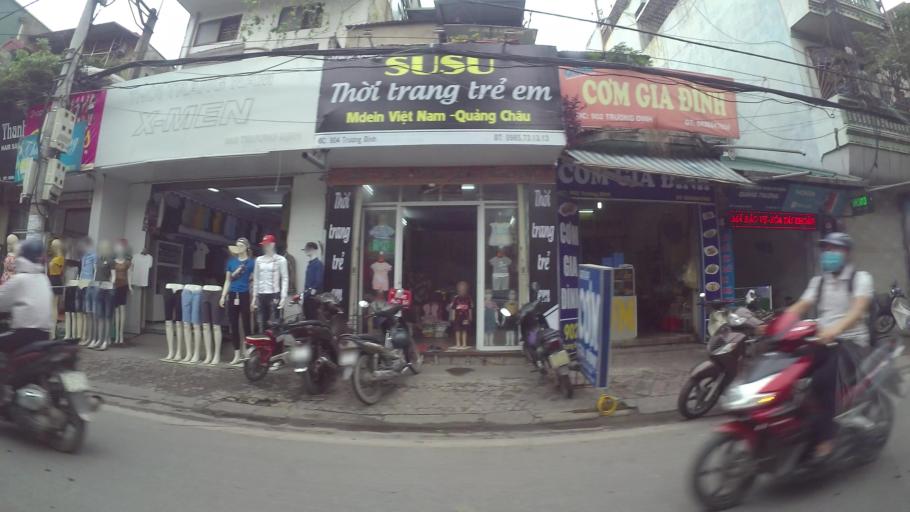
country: VN
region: Ha Noi
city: Van Dien
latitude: 20.9777
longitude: 105.8420
